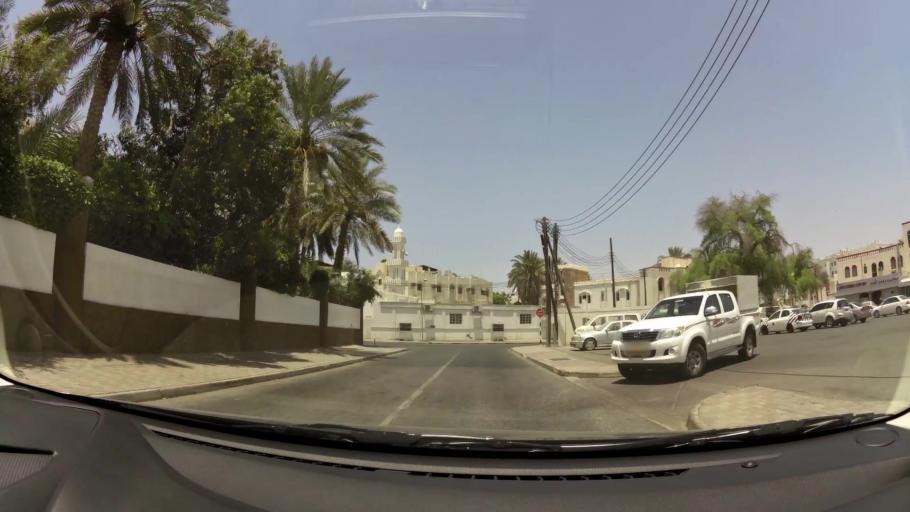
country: OM
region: Muhafazat Masqat
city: Muscat
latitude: 23.6200
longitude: 58.4950
